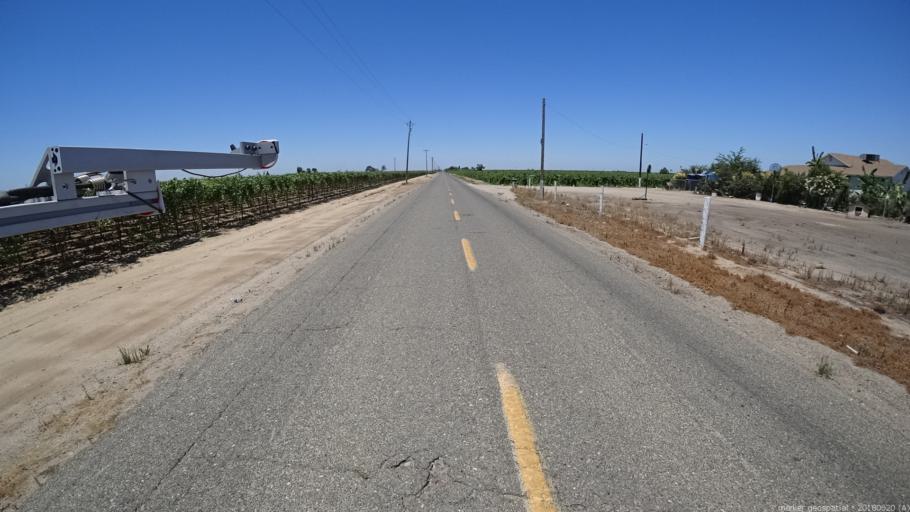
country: US
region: California
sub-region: Madera County
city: Parkwood
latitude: 36.8658
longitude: -120.0301
